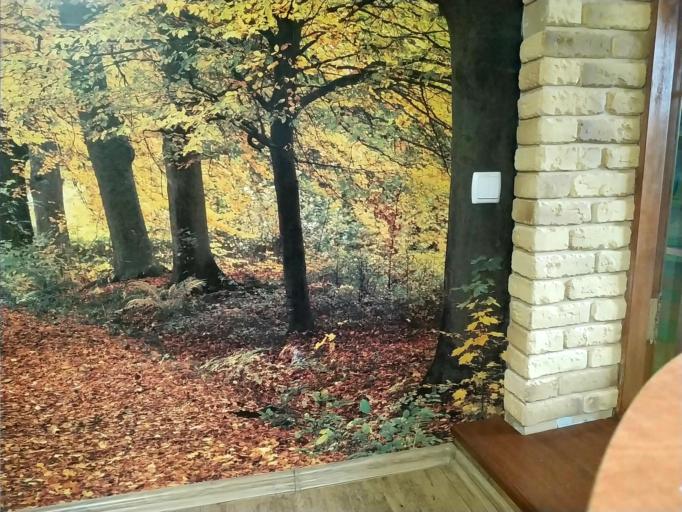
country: RU
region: Smolensk
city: Verkhnedneprovskiy
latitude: 54.9834
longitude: 33.2760
